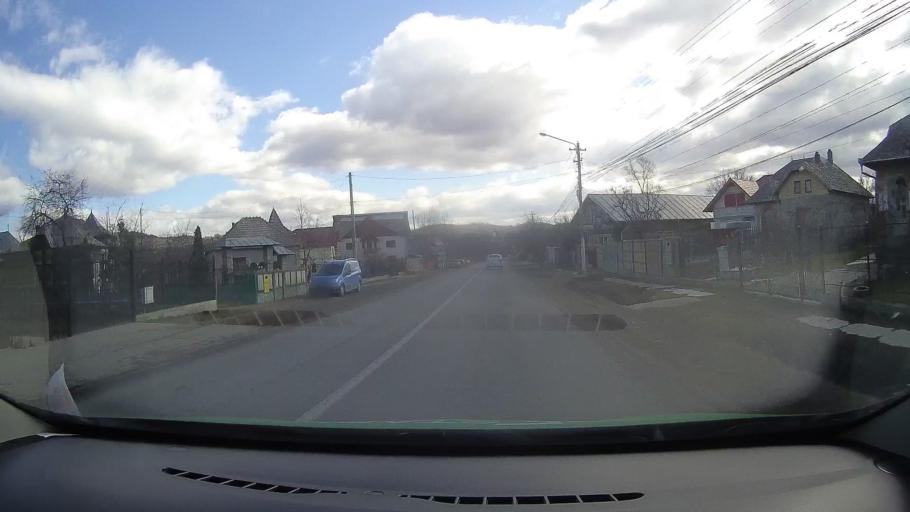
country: RO
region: Dambovita
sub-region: Comuna Motaeni
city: Motaeni
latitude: 45.0945
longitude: 25.4186
